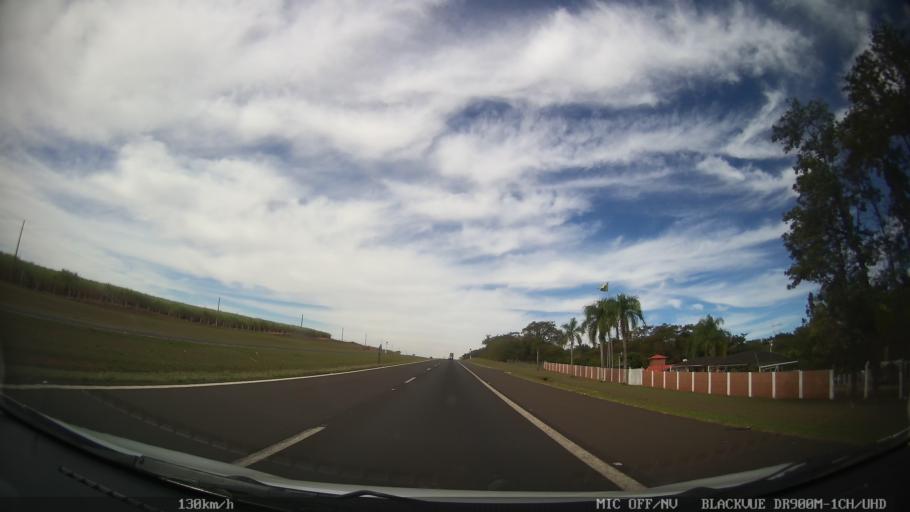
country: BR
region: Sao Paulo
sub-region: Matao
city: Matao
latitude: -21.5550
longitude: -48.4834
